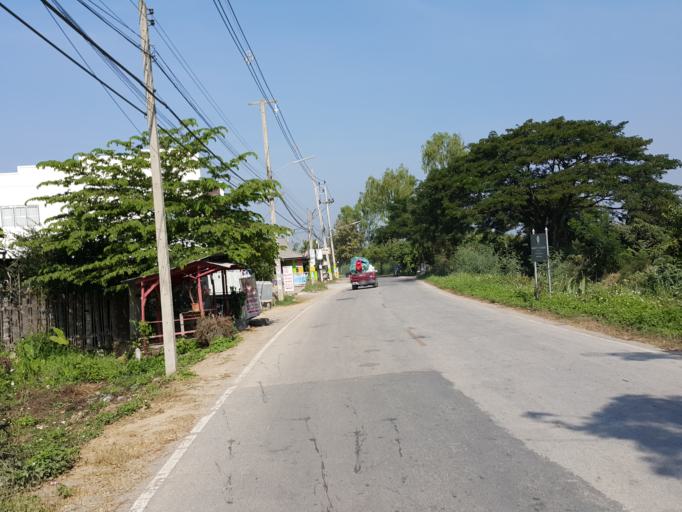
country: TH
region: Lamphun
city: Lamphun
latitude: 18.6047
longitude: 99.0087
